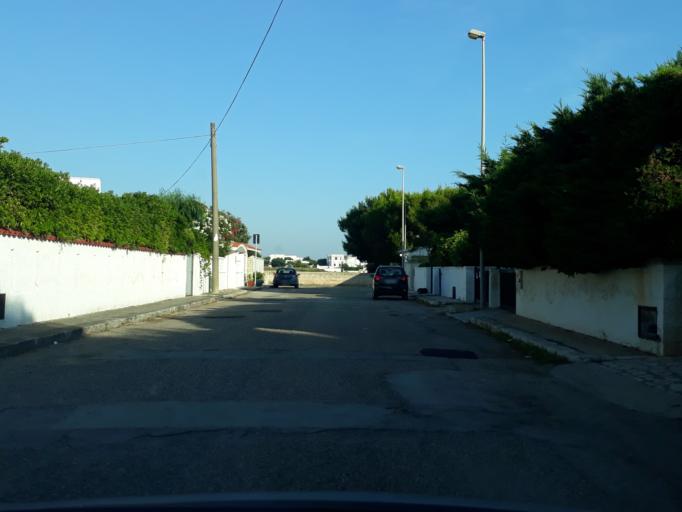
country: IT
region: Apulia
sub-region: Provincia di Brindisi
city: Carovigno
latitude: 40.7599
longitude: 17.6936
